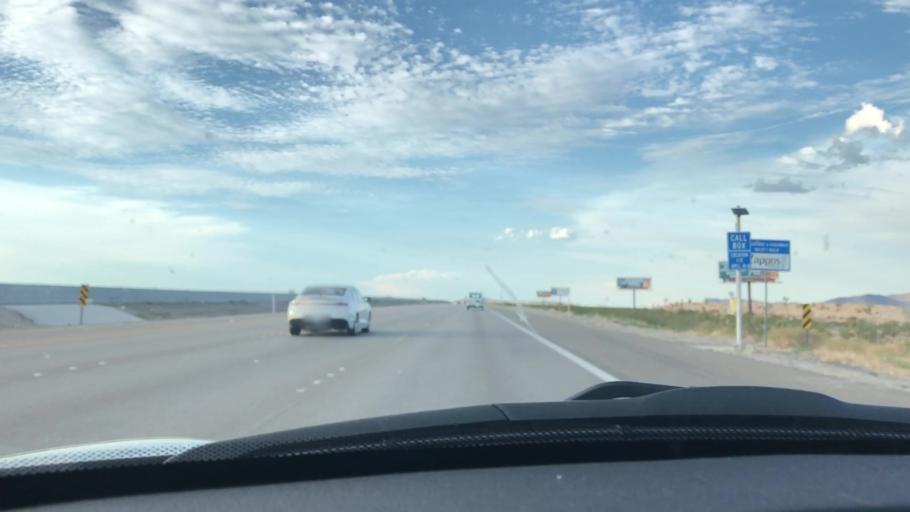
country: US
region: Nevada
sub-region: Clark County
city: Enterprise
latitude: 35.8101
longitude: -115.3066
